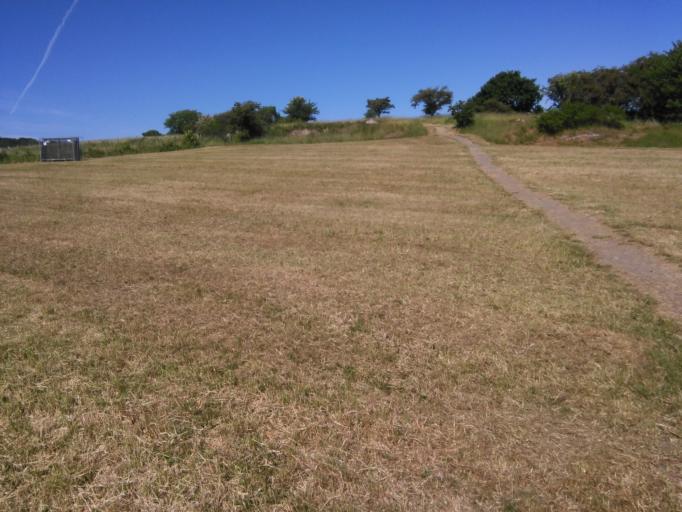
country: DK
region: Capital Region
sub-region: Bornholm Kommune
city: Ronne
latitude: 55.2807
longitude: 14.7902
